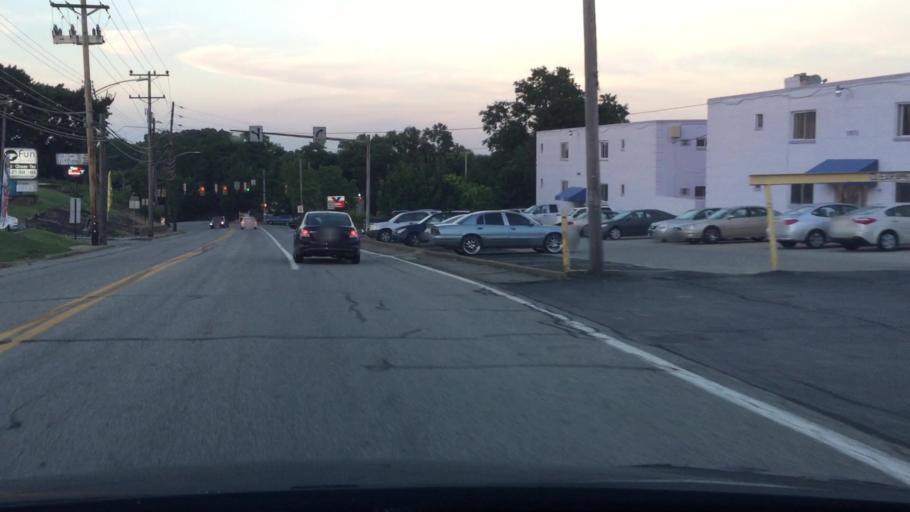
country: US
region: Pennsylvania
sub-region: Allegheny County
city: Churchill
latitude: 40.4654
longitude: -79.8274
